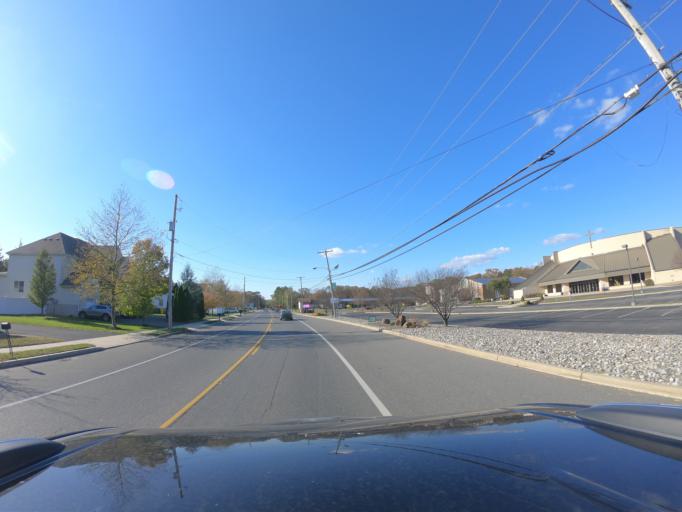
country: US
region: New Jersey
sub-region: Monmouth County
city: Ramtown
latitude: 40.1035
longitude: -74.1748
